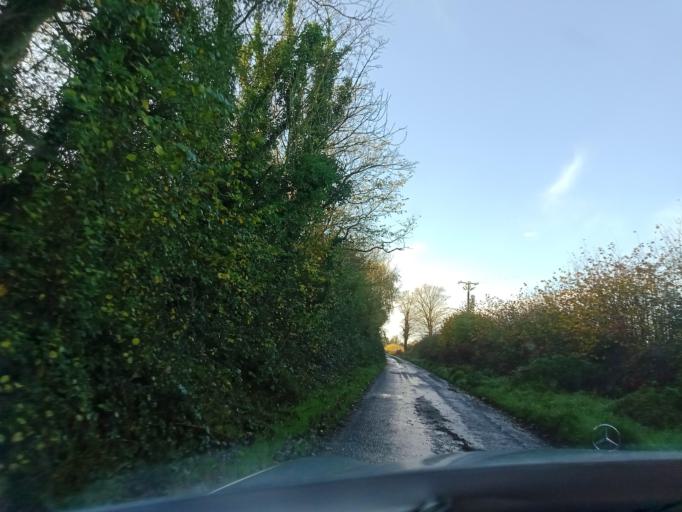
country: IE
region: Leinster
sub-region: Kilkenny
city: Mooncoin
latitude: 52.2910
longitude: -7.1877
